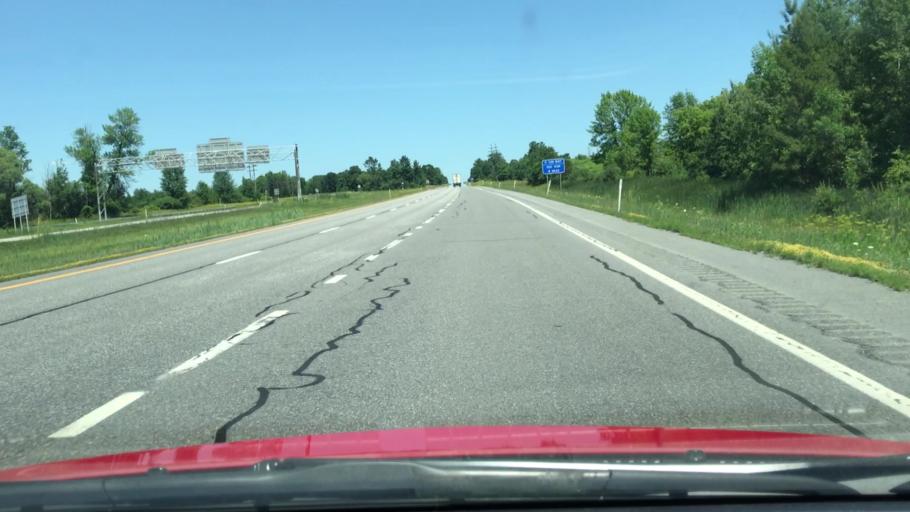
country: US
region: New York
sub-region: Clinton County
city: Plattsburgh
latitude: 44.7312
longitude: -73.4378
